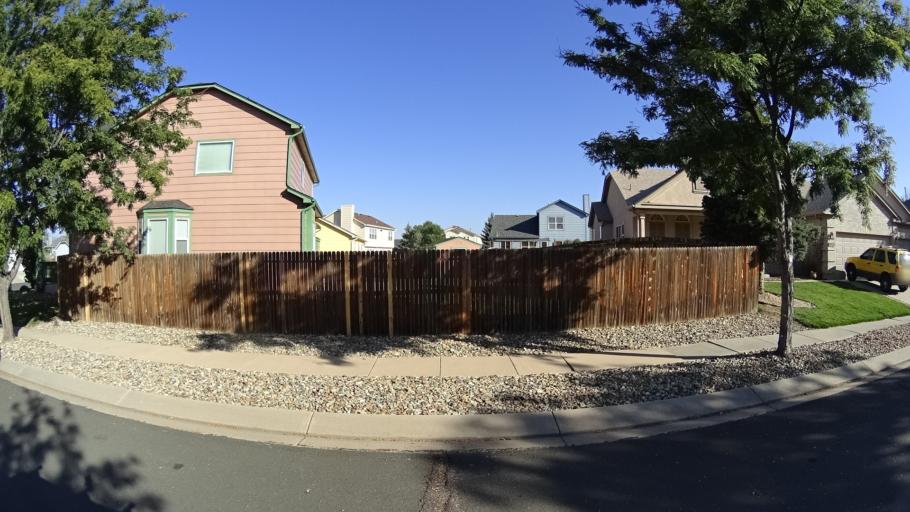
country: US
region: Colorado
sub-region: El Paso County
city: Cimarron Hills
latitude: 38.8818
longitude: -104.6981
